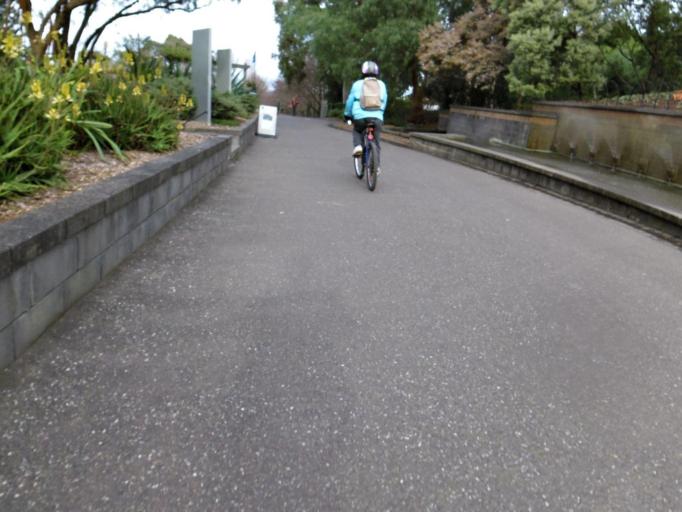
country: AU
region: Victoria
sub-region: Casey
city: Berwick
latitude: -38.0272
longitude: 145.3368
